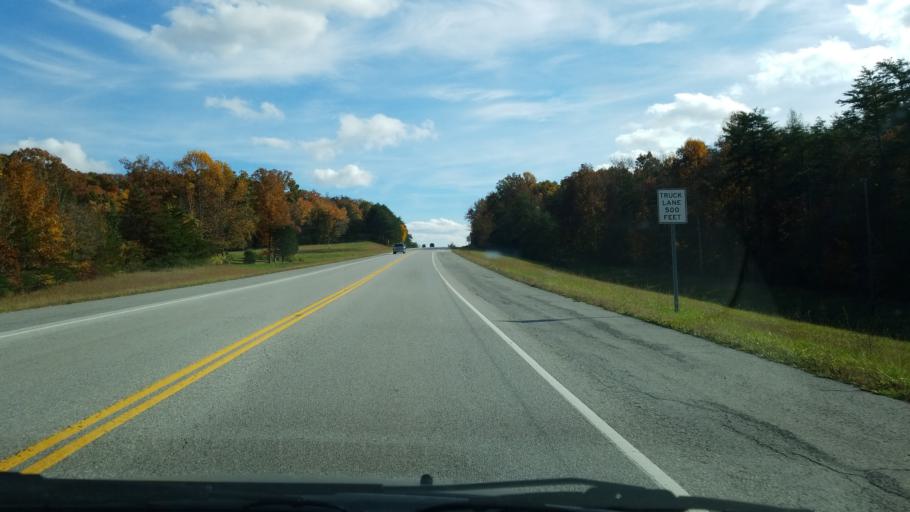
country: US
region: Tennessee
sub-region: Sequatchie County
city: Dunlap
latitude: 35.4634
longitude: -85.4450
